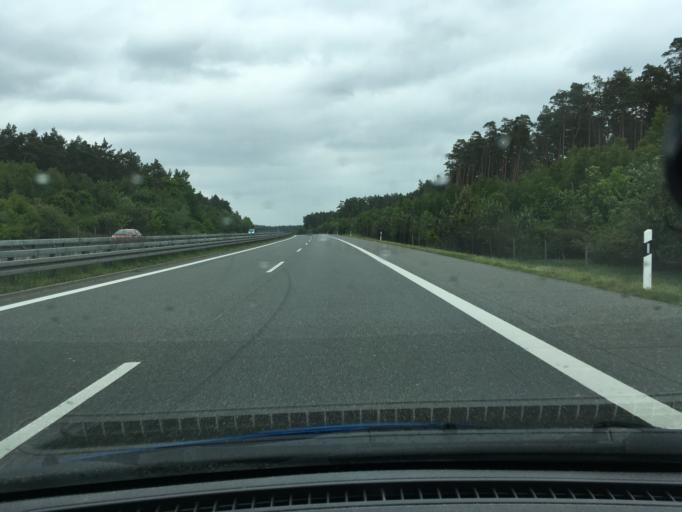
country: DE
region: Schleswig-Holstein
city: Gross Gronau
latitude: 53.8056
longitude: 10.7752
